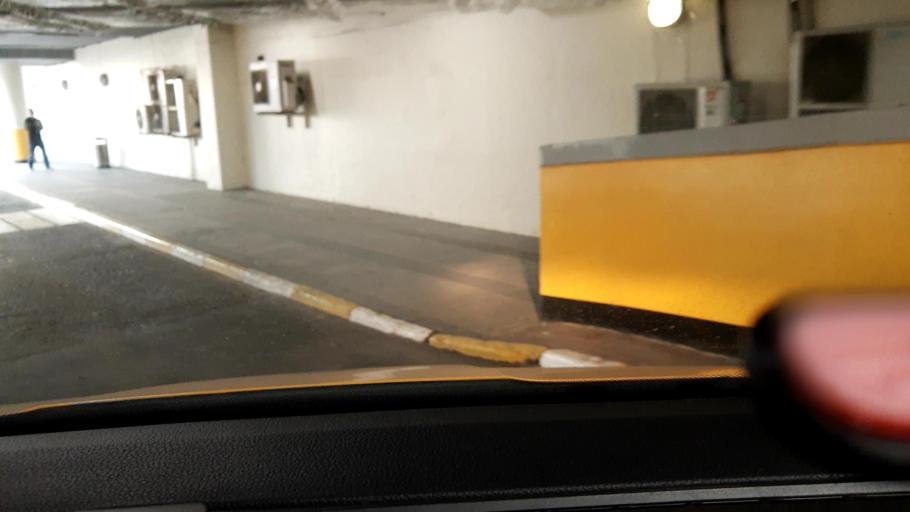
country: RU
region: Moskovskaya
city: Semenovskoye
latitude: 55.6918
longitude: 37.5288
